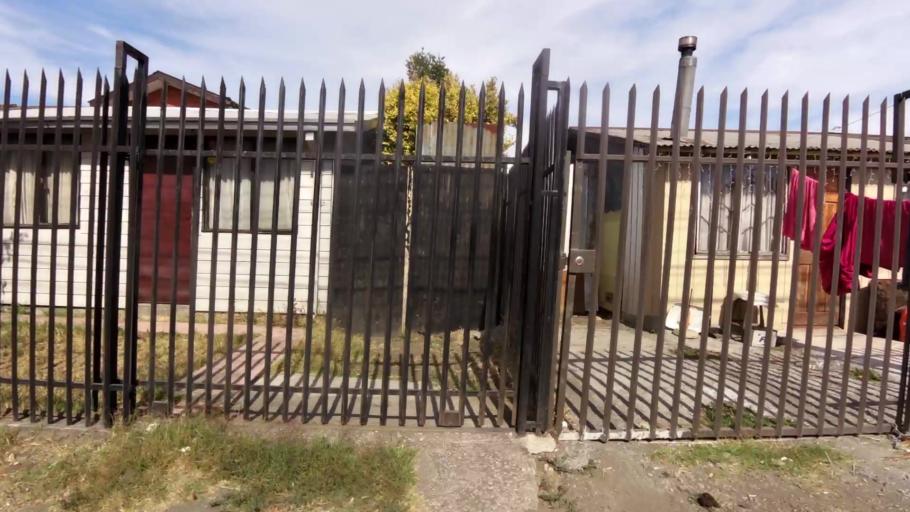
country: CL
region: Biobio
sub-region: Provincia de Concepcion
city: Talcahuano
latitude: -36.7788
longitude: -73.1068
